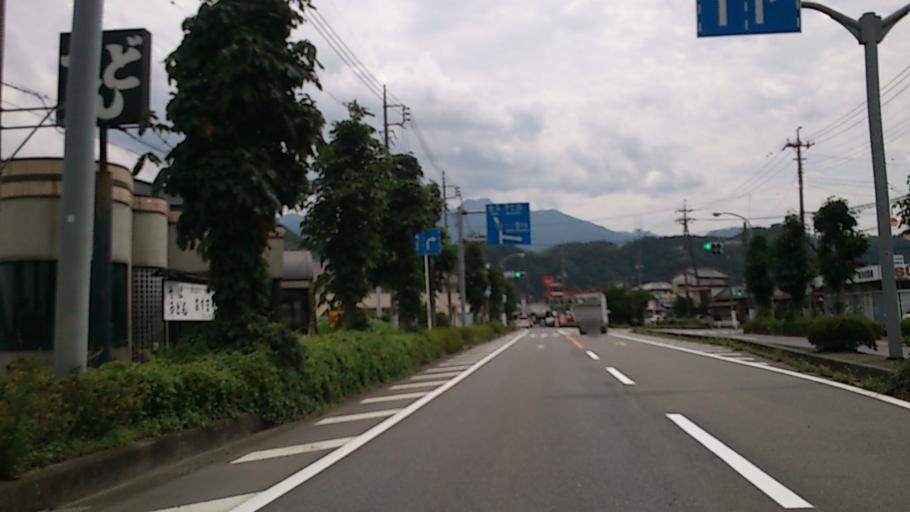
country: JP
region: Gunma
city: Tomioka
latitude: 36.2489
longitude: 138.8598
